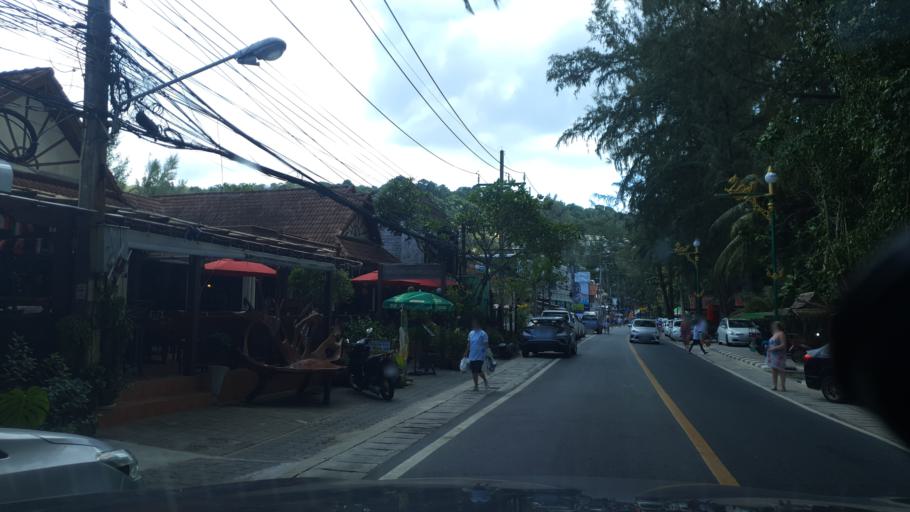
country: TH
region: Phuket
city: Thalang
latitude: 8.0594
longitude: 98.2780
